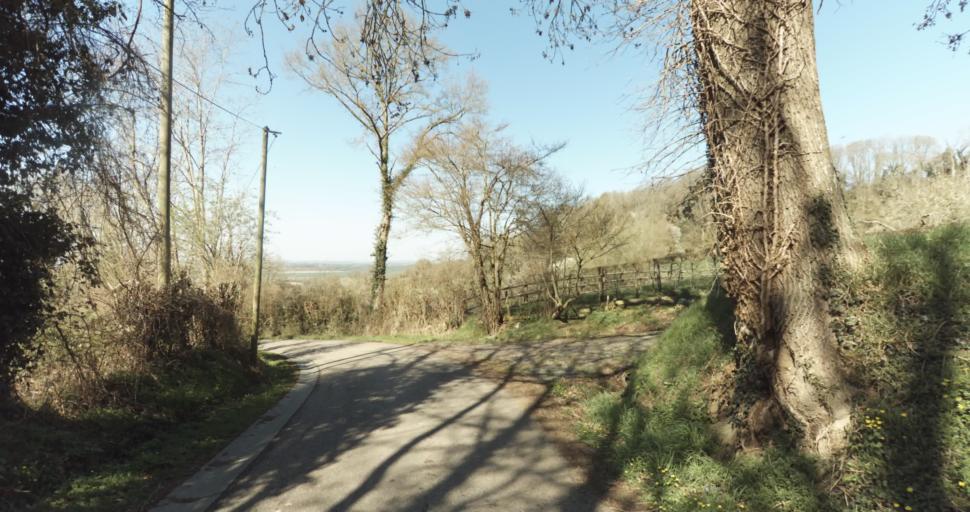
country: FR
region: Lower Normandy
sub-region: Departement du Calvados
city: Saint-Pierre-sur-Dives
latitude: 48.9900
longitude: 0.0458
